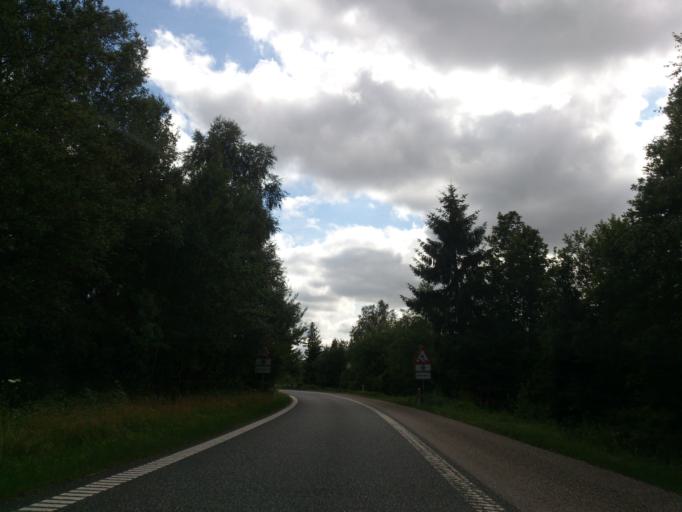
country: DK
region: South Denmark
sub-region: Aabenraa Kommune
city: Krusa
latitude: 54.8787
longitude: 9.3775
